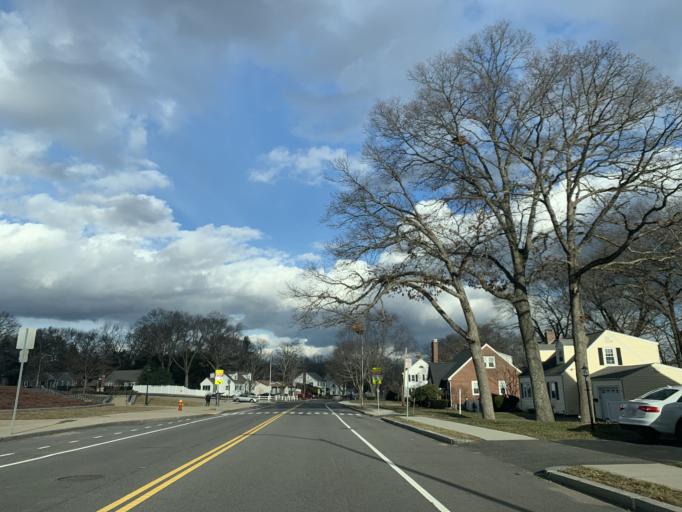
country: US
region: Massachusetts
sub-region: Norfolk County
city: Norwood
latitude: 42.1903
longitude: -71.2139
